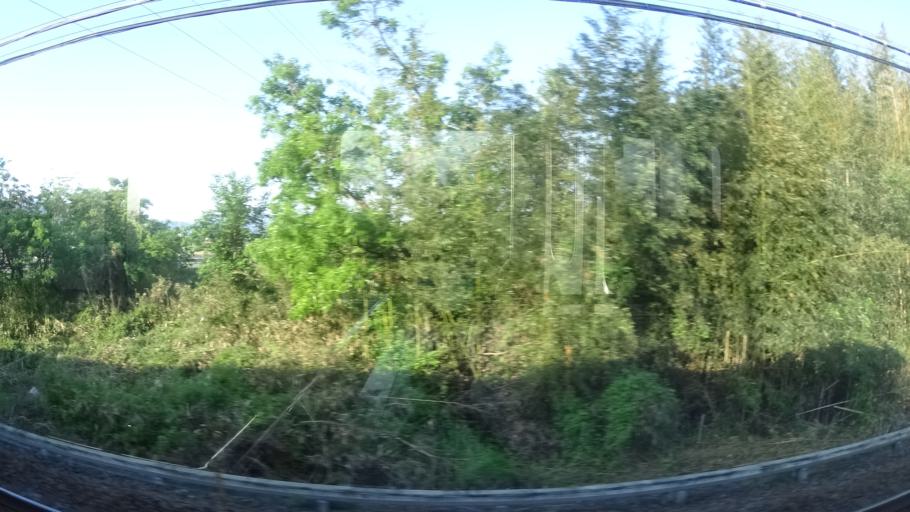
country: JP
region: Mie
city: Ise
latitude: 34.5080
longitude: 136.6912
